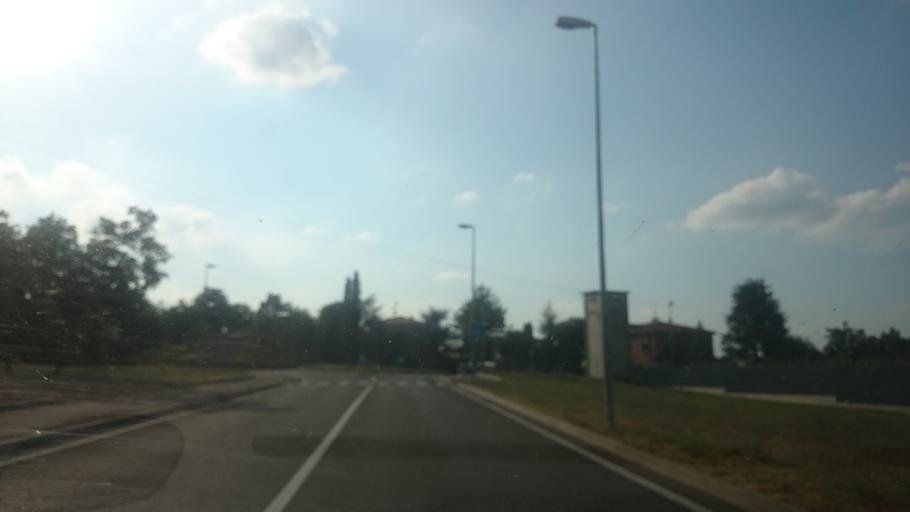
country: IT
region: Emilia-Romagna
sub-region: Provincia di Reggio Emilia
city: Salvaterra
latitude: 44.5899
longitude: 10.7579
